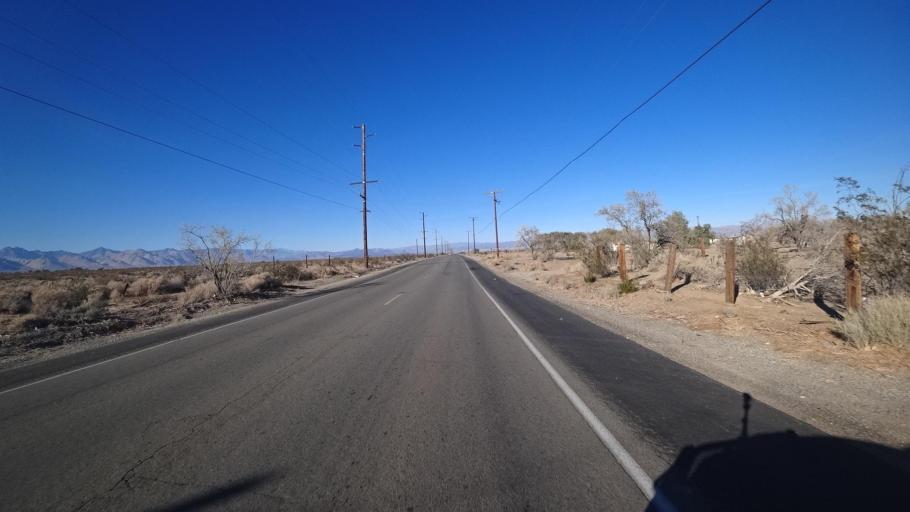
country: US
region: California
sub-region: Kern County
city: China Lake Acres
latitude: 35.6350
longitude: -117.7229
